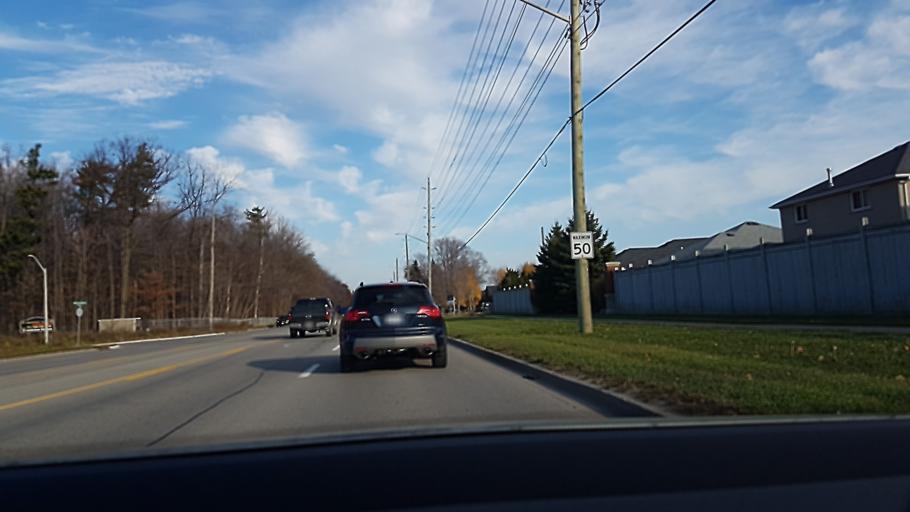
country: CA
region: Ontario
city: Barrie
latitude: 44.3629
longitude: -79.6215
